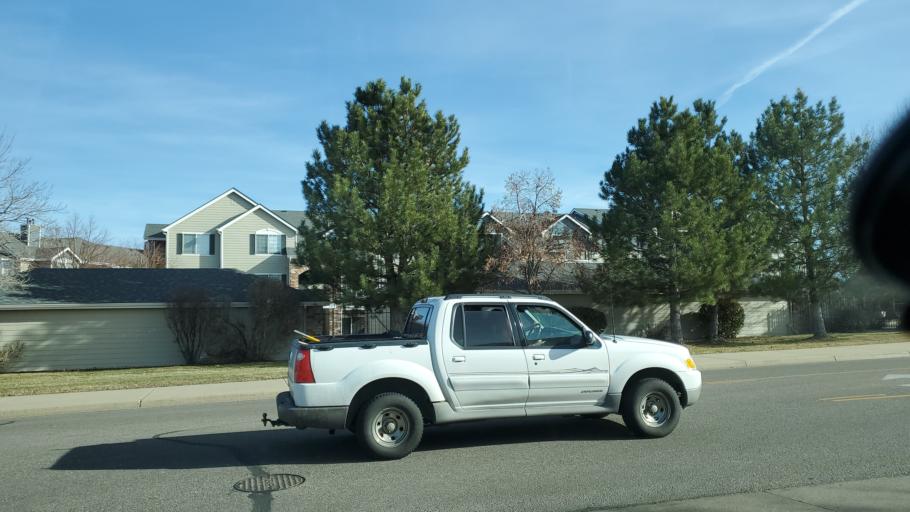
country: US
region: Colorado
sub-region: Adams County
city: Northglenn
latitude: 39.9152
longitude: -104.9535
